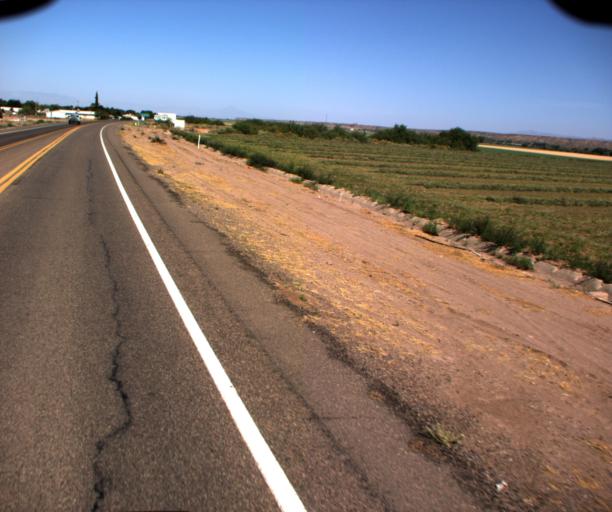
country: US
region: Arizona
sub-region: Graham County
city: Safford
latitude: 32.8133
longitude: -109.6190
